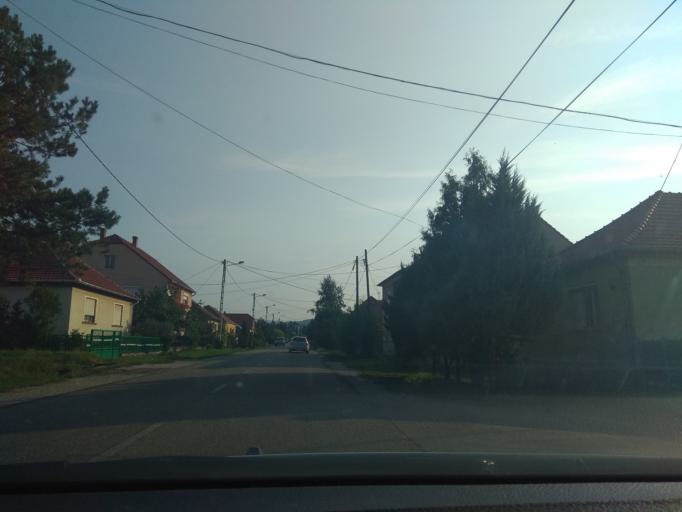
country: HU
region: Heves
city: Felsotarkany
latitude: 47.9659
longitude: 20.4061
